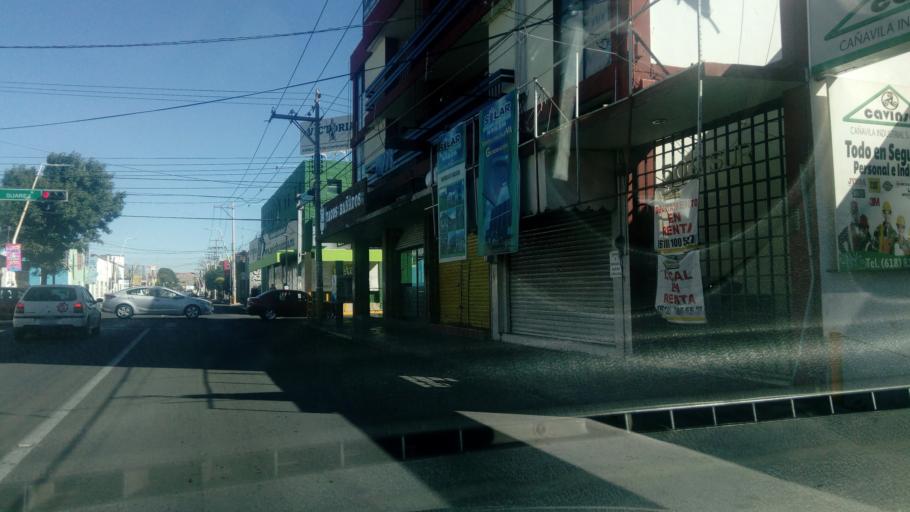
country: MX
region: Durango
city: Victoria de Durango
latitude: 24.0246
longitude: -104.6524
